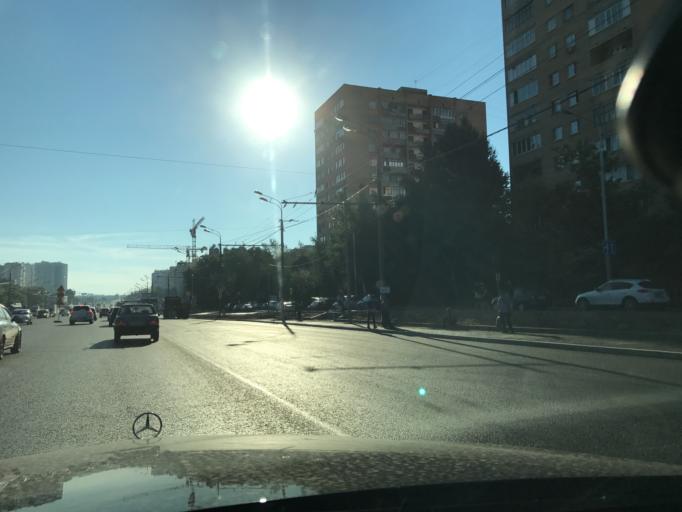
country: RU
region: Moscow
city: Gol'yanovo
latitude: 55.8113
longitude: 37.8168
